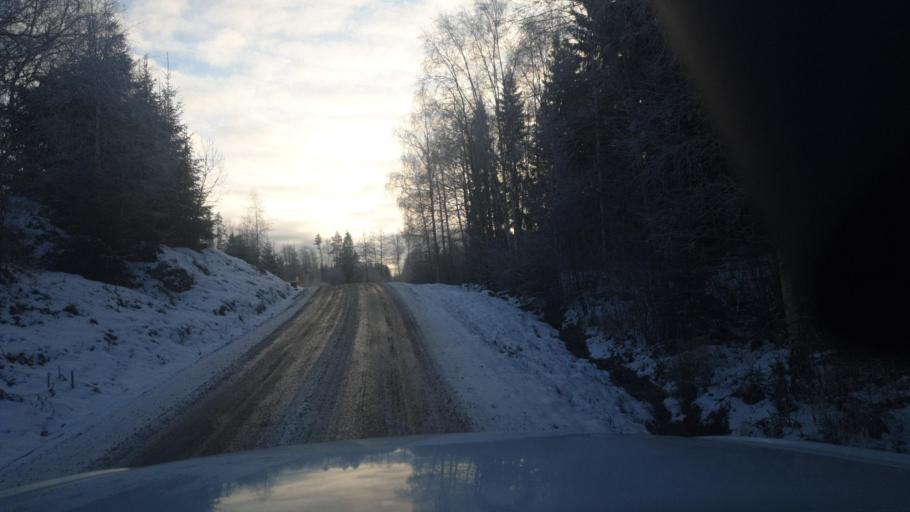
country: SE
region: Vaermland
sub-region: Arvika Kommun
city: Arvika
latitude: 60.0069
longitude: 12.6581
